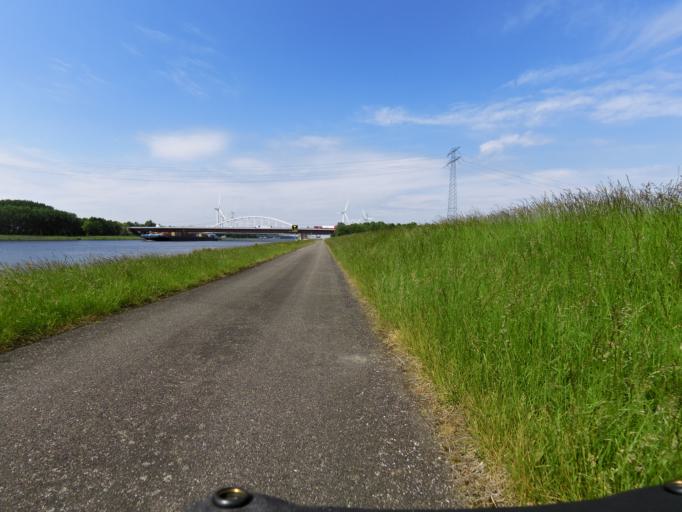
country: NL
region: North Brabant
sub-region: Gemeente Woensdrecht
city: Woensdrecht
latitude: 51.4243
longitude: 4.2365
